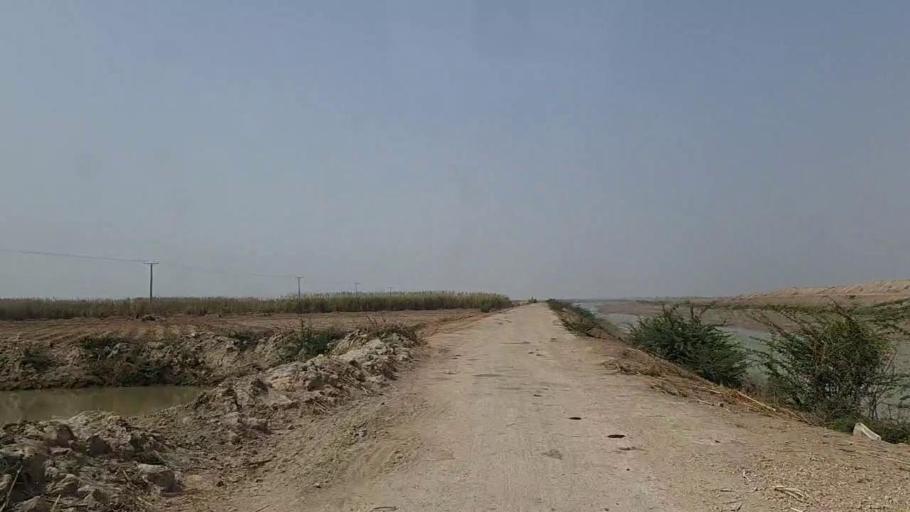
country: PK
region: Sindh
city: Naukot
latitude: 24.7970
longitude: 69.3412
